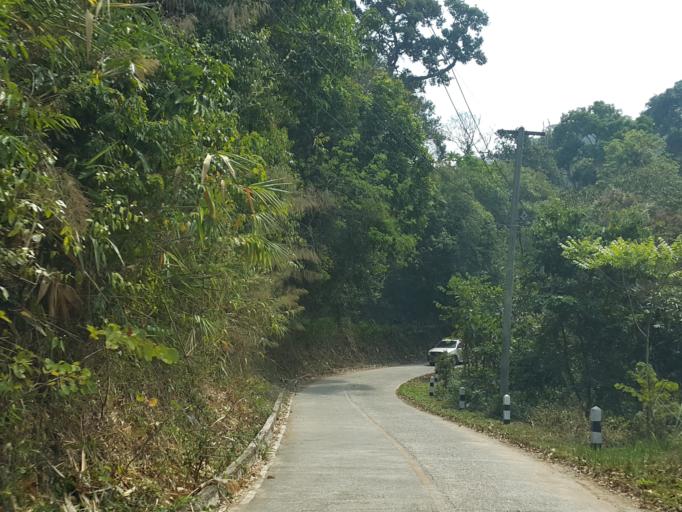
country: TH
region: Lampang
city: Mueang Pan
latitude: 18.8271
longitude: 99.4083
